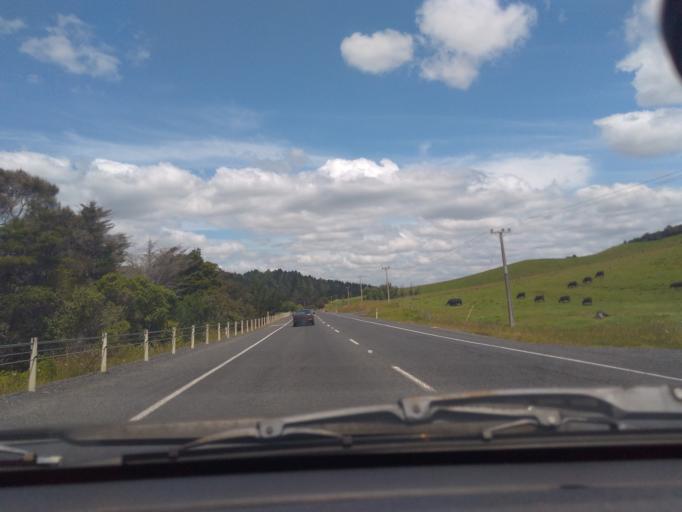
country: NZ
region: Northland
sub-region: Far North District
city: Kerikeri
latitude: -35.2771
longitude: 173.9519
